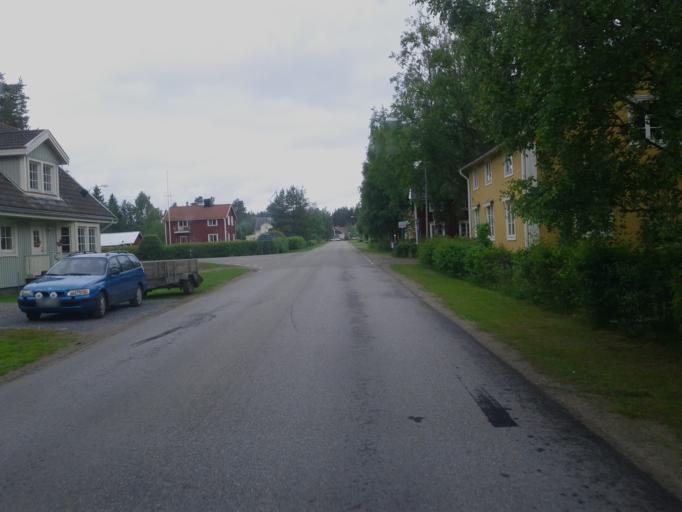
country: SE
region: Vaesterbotten
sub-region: Skelleftea Kommun
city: Kage
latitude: 64.9192
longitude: 20.9510
